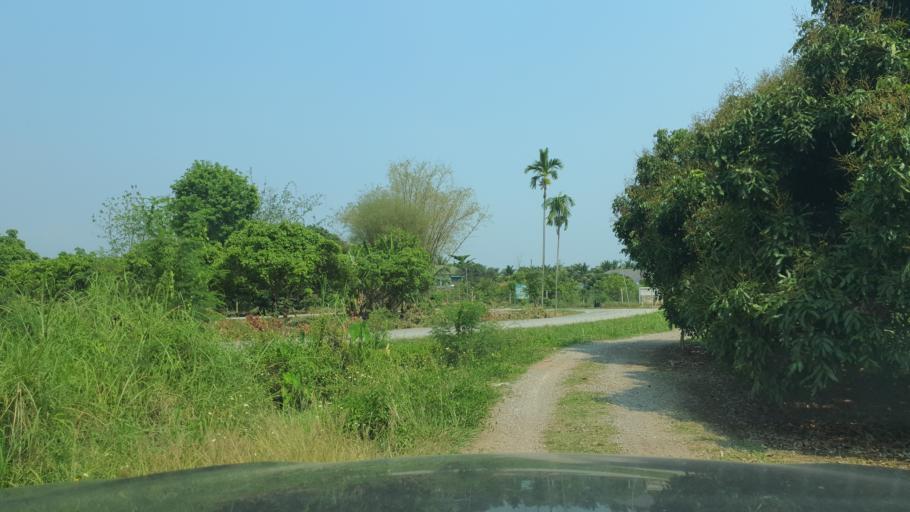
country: TH
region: Chiang Mai
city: Saraphi
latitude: 18.6710
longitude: 98.9973
